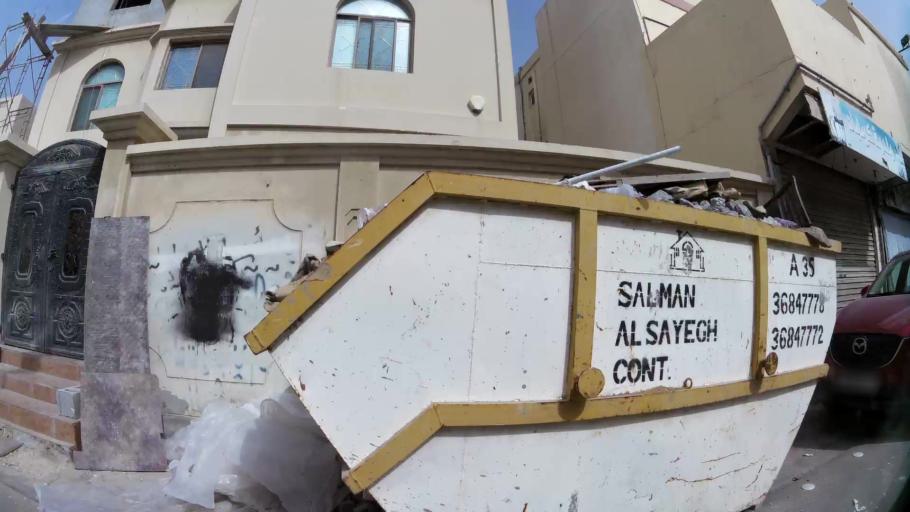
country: BH
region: Manama
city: Jidd Hafs
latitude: 26.2317
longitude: 50.5298
